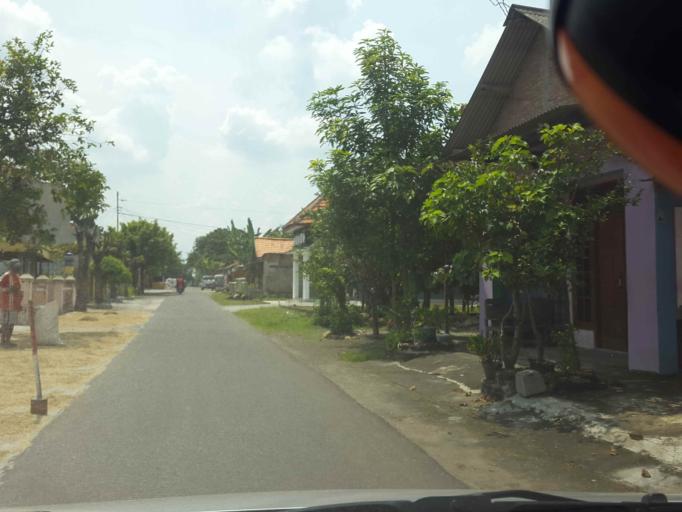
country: ID
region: Central Java
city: Sragen
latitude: -7.3471
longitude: 110.8380
